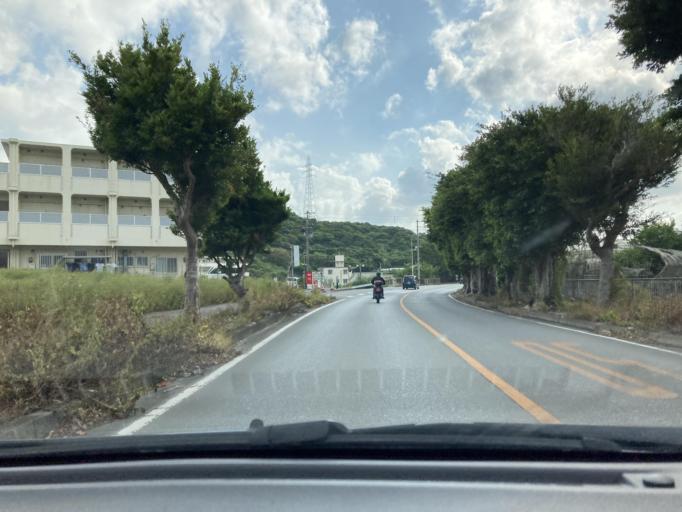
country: JP
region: Okinawa
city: Tomigusuku
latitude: 26.1658
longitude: 127.7356
